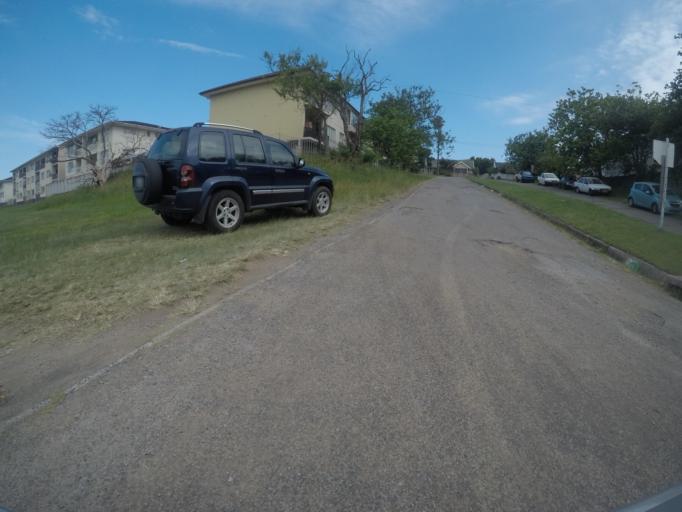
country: ZA
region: Eastern Cape
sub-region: Buffalo City Metropolitan Municipality
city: East London
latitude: -32.9831
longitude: 27.8937
